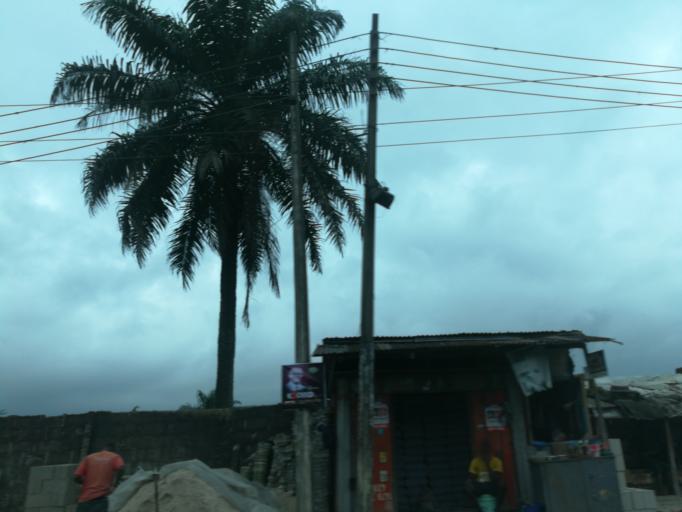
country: NG
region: Rivers
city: Port Harcourt
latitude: 4.8129
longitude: 7.0178
